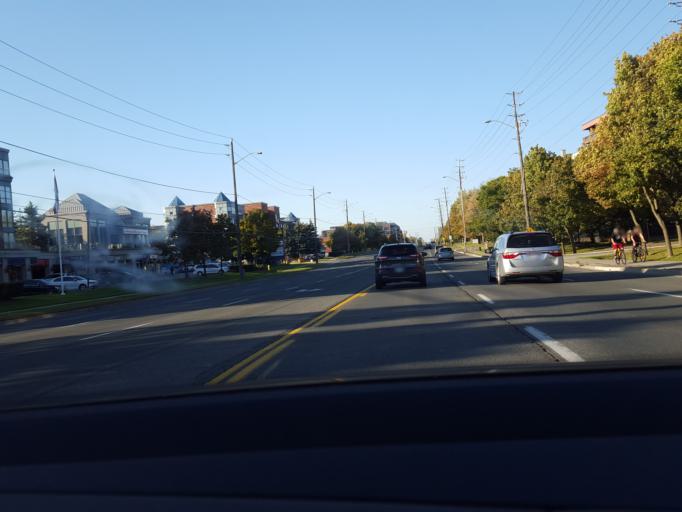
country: CA
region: Ontario
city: North York
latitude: 43.8077
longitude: -79.4225
